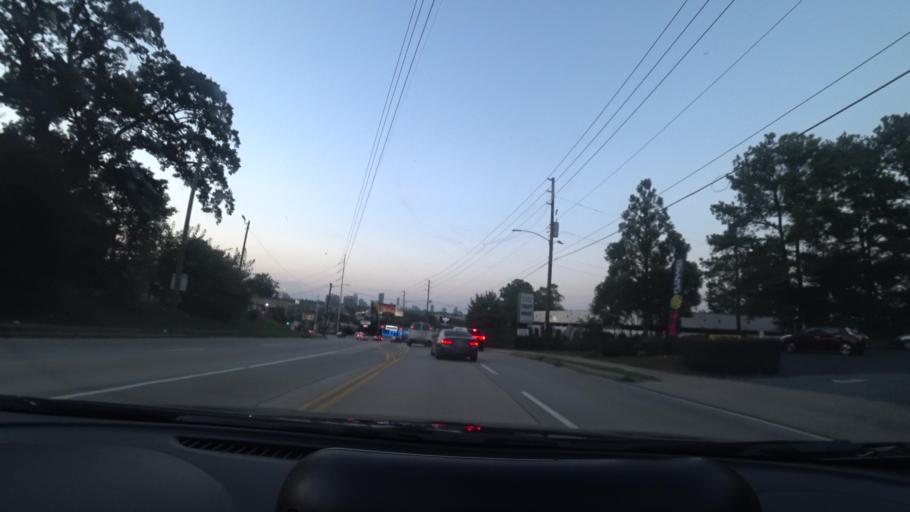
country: US
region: Georgia
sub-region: DeKalb County
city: Druid Hills
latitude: 33.8087
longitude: -84.3658
